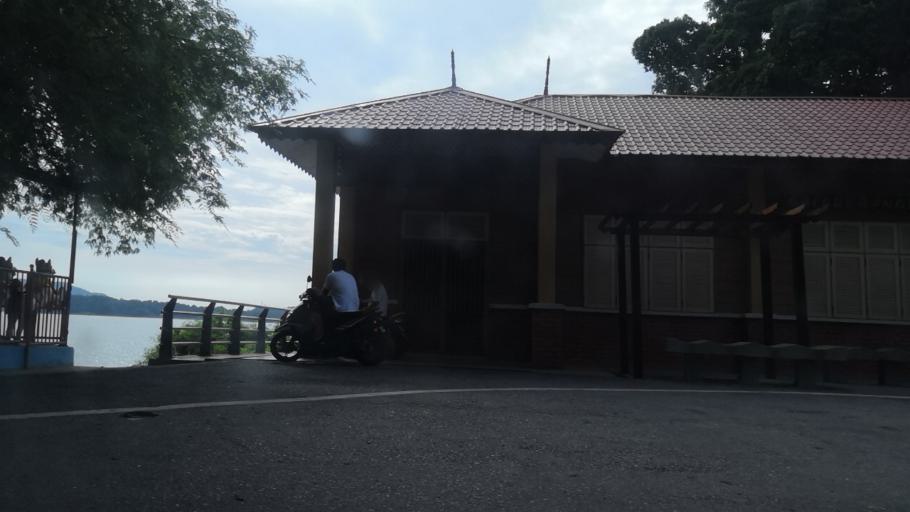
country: MY
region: Perak
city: Lumut
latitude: 4.2153
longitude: 100.5769
